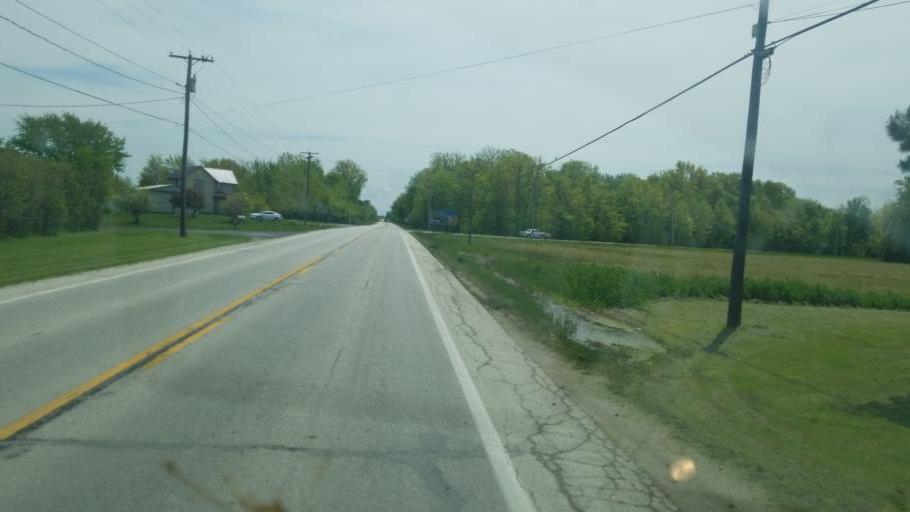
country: US
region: Ohio
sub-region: Ottawa County
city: Oak Harbor
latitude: 41.5555
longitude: -83.0688
